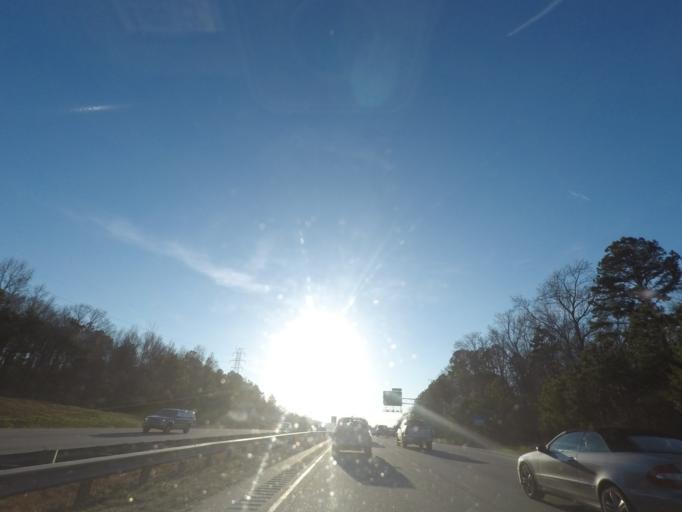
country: US
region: North Carolina
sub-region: Durham County
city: Gorman
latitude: 36.0198
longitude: -78.8584
